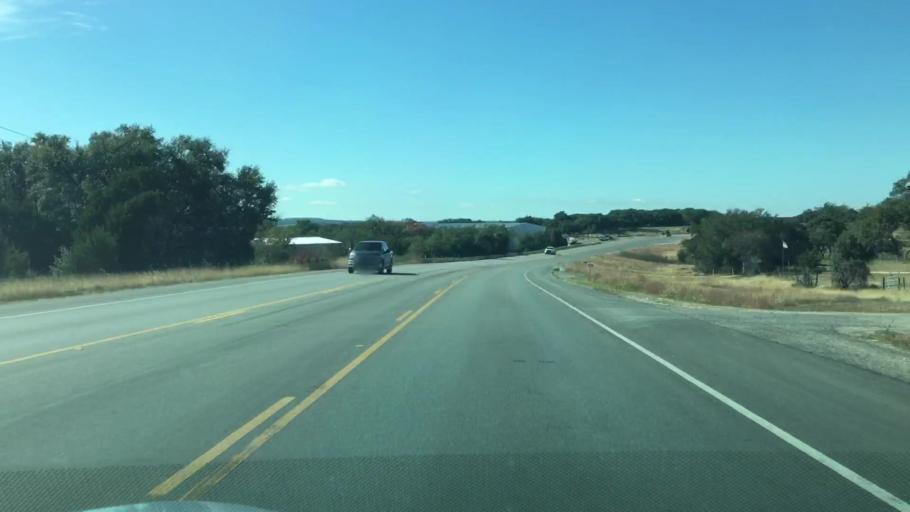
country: US
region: Texas
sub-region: Hays County
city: Dripping Springs
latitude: 30.2075
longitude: -98.1466
